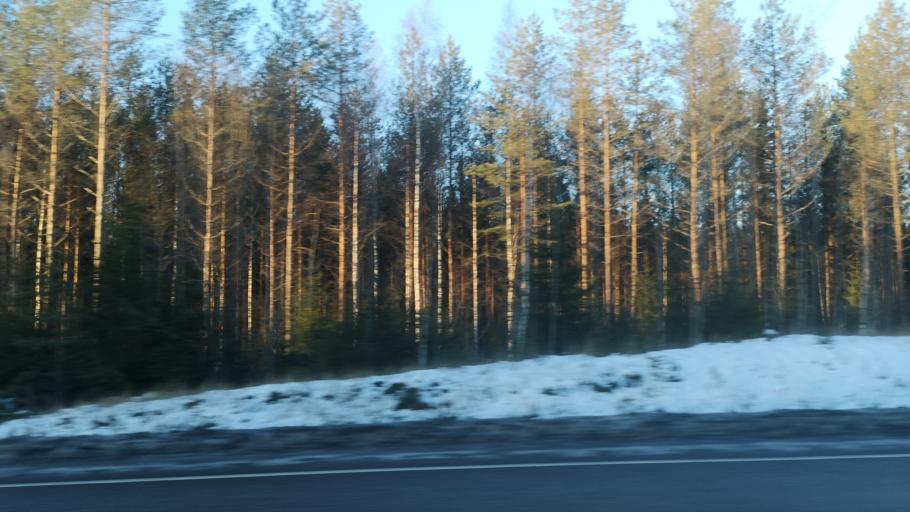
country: FI
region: Southern Savonia
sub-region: Pieksaemaeki
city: Juva
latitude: 61.8858
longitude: 27.7911
